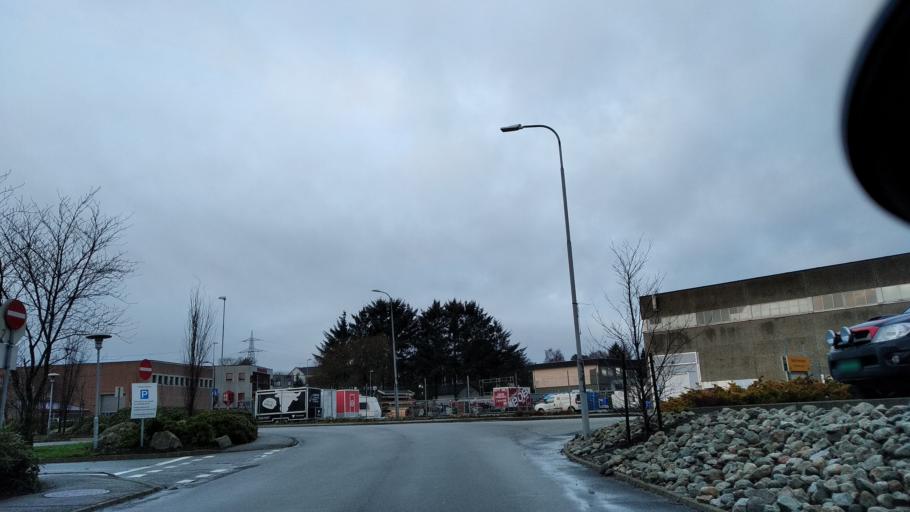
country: NO
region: Rogaland
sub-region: Randaberg
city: Randaberg
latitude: 58.9505
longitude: 5.6554
